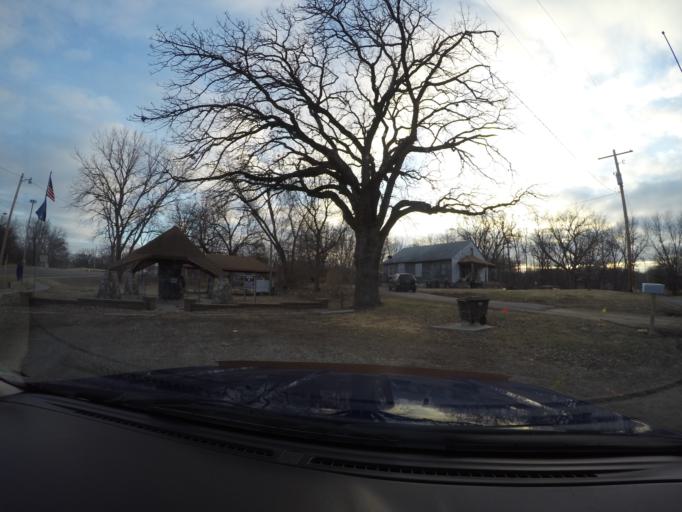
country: US
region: Kansas
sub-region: Morris County
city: Council Grove
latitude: 38.6559
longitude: -96.4884
